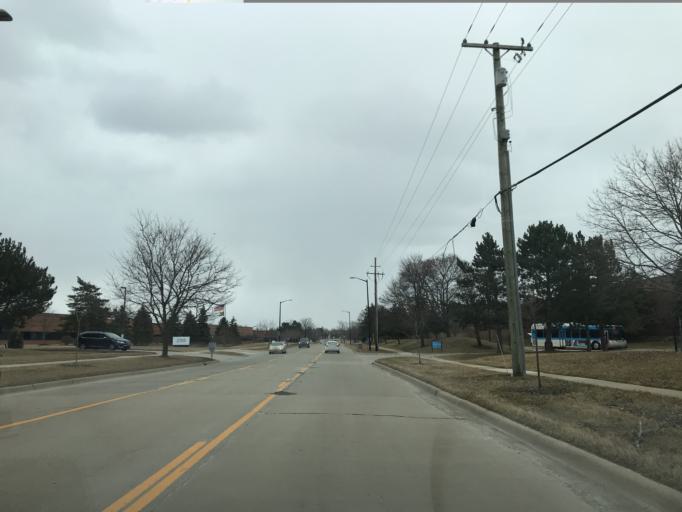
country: US
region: Michigan
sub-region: Washtenaw County
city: Ann Arbor
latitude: 42.2492
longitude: -83.7319
